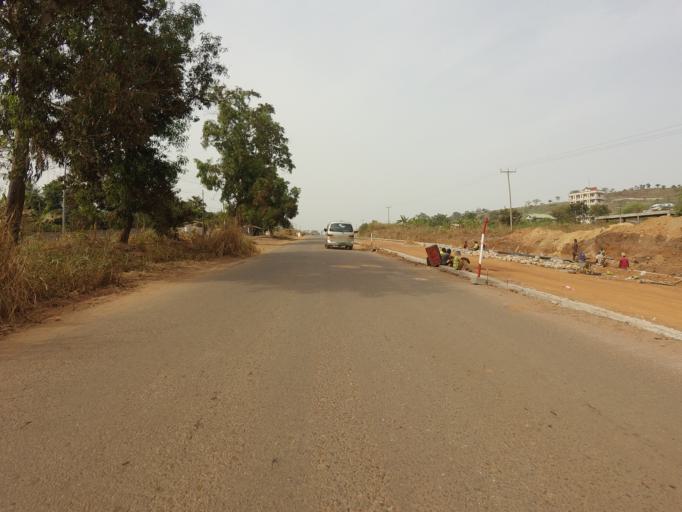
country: GH
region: Volta
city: Ho
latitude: 6.5940
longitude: 0.4390
